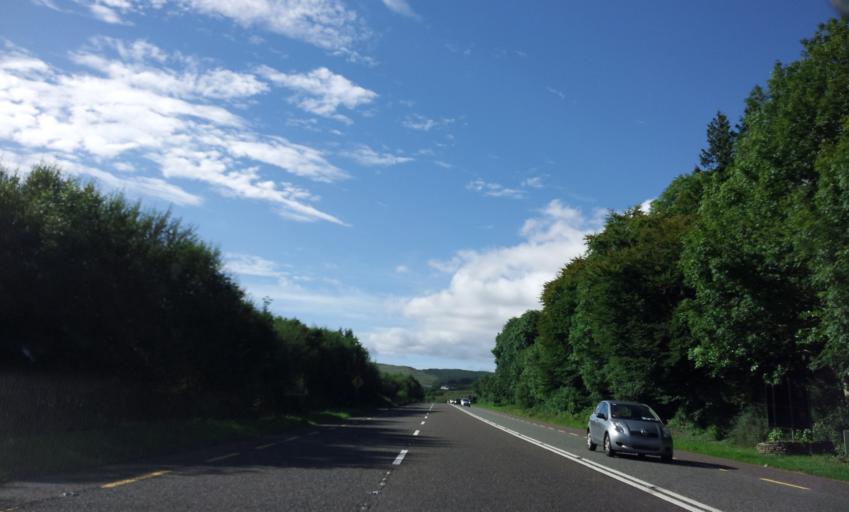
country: IE
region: Munster
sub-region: County Cork
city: Millstreet
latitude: 51.9537
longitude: -9.1860
